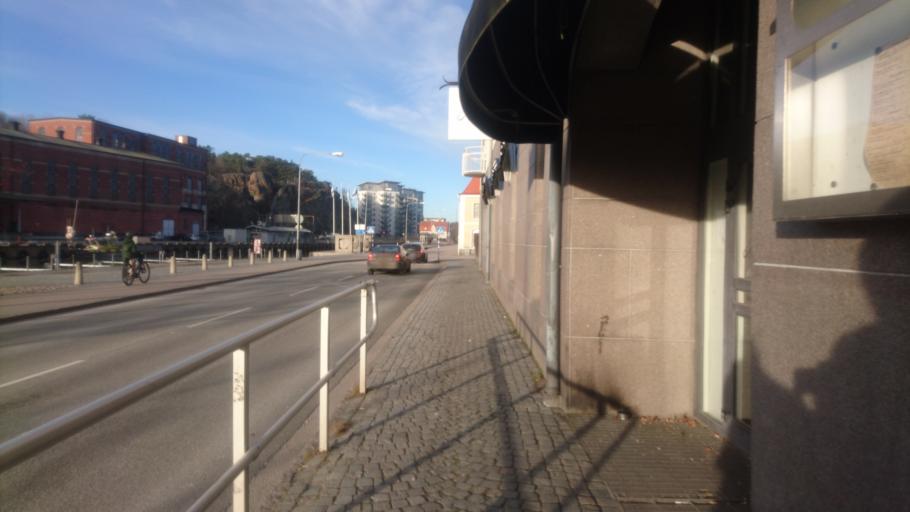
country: SE
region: Blekinge
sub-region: Karlshamns Kommun
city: Karlshamn
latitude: 56.1680
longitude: 14.8622
